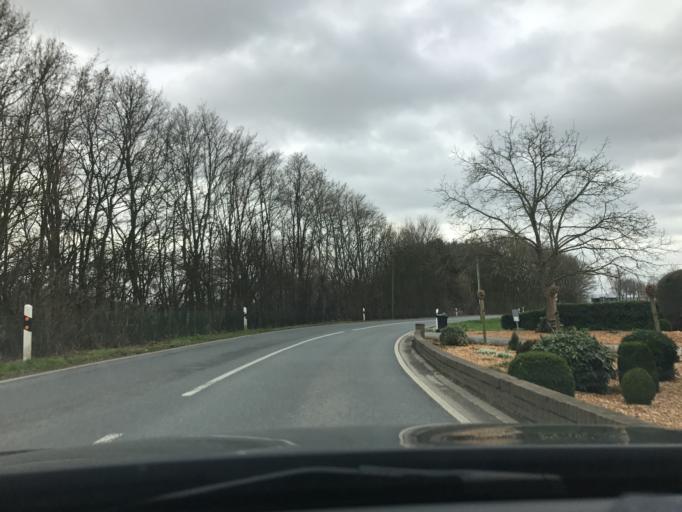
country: DE
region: North Rhine-Westphalia
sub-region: Regierungsbezirk Dusseldorf
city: Wachtendonk
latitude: 51.4183
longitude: 6.3423
